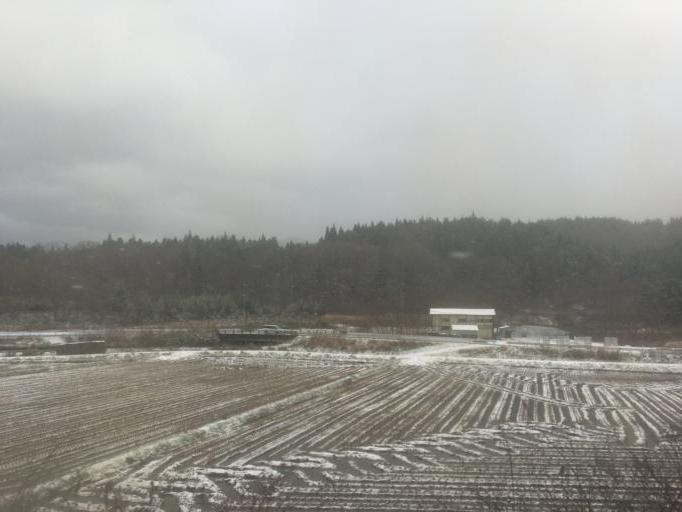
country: JP
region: Aomori
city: Goshogawara
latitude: 41.1335
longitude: 140.5181
